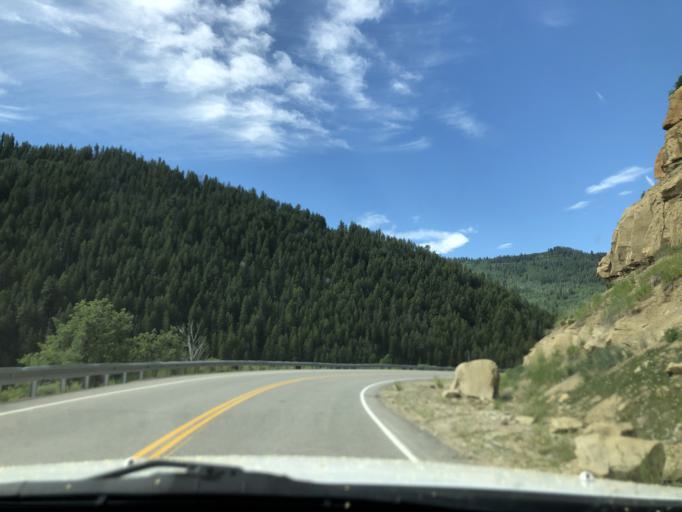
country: US
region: Colorado
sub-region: Delta County
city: Paonia
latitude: 38.9440
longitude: -107.3500
